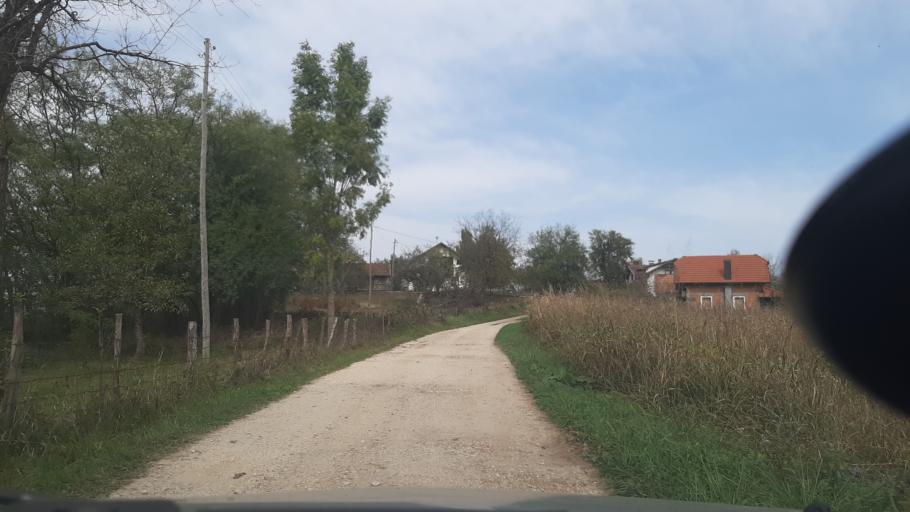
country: BA
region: Republika Srpska
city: Maglajani
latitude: 44.8782
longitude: 17.4732
